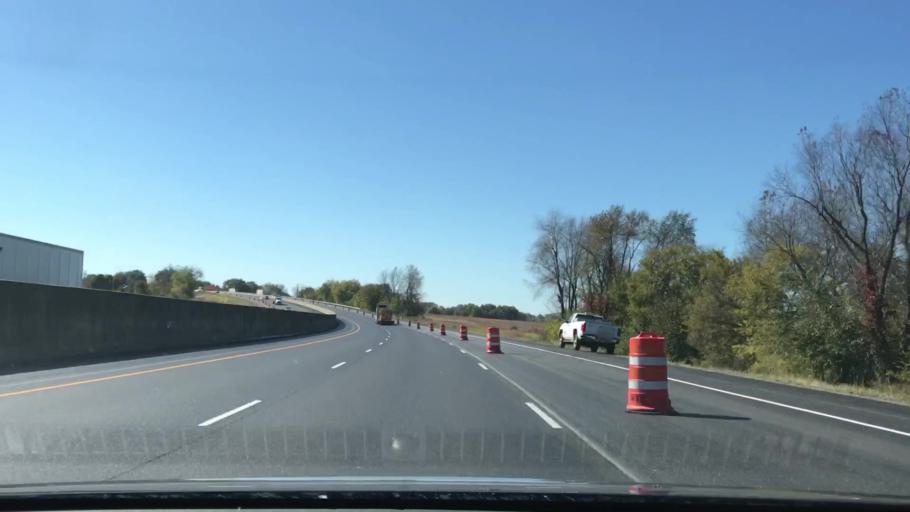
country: US
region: Kentucky
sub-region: Edmonson County
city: Brownsville
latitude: 37.0363
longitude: -86.2360
